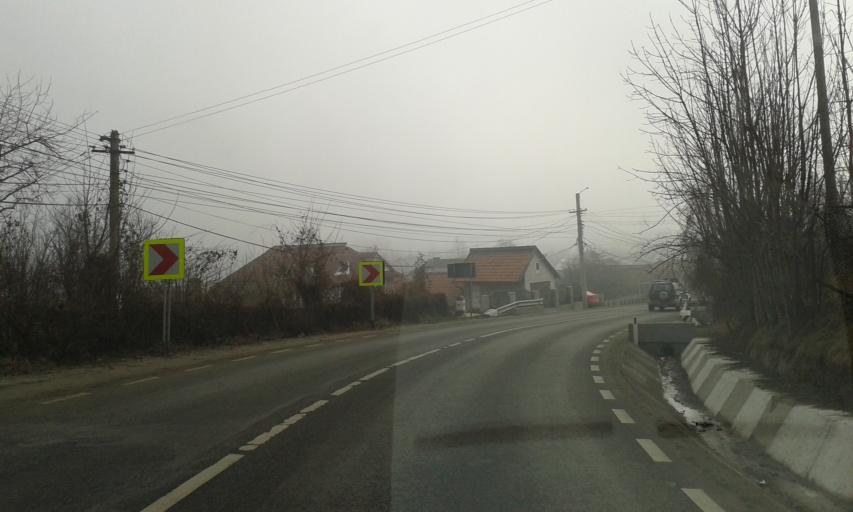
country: RO
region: Hunedoara
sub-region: Comuna Aninoasa
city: Iscroni
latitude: 45.3783
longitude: 23.3303
